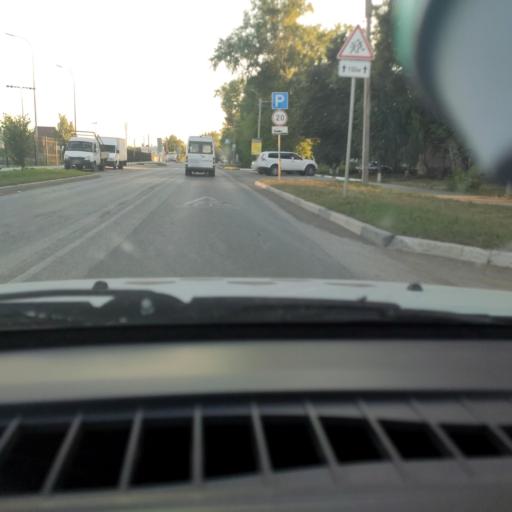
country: RU
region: Perm
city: Kungur
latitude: 57.4368
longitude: 56.9543
